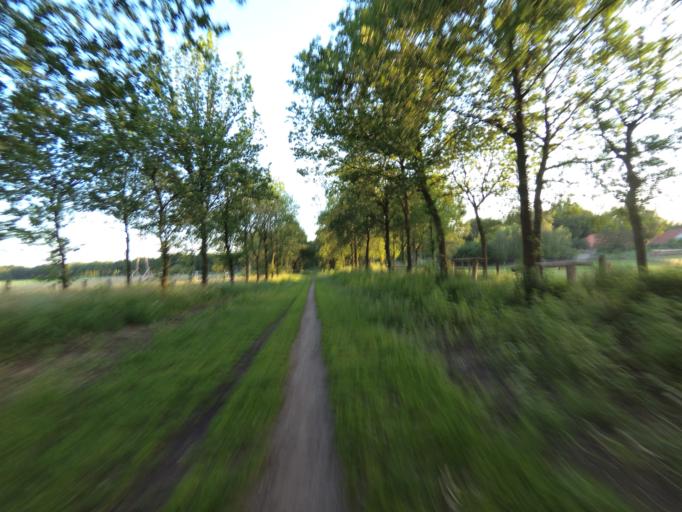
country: NL
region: Gelderland
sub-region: Gemeente Apeldoorn
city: Beekbergen
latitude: 52.1239
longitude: 5.8826
